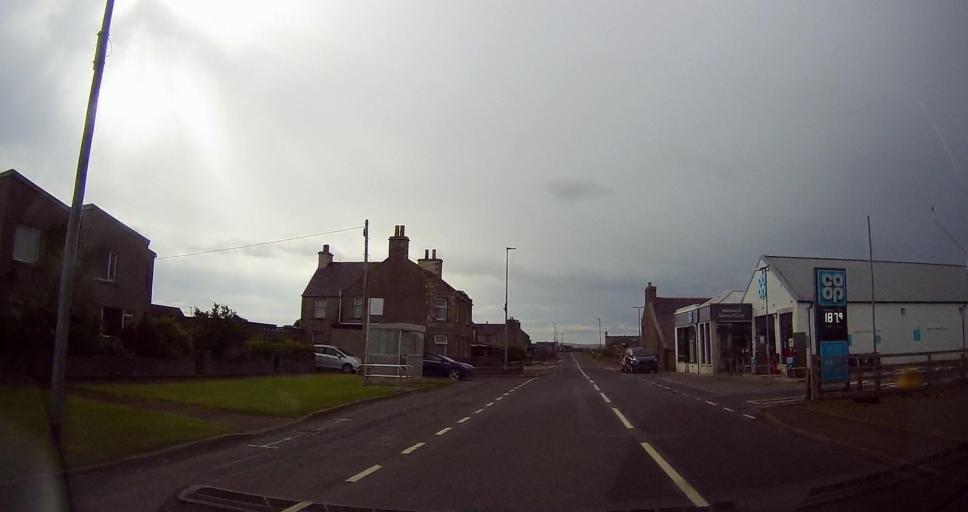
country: GB
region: Scotland
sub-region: Orkney Islands
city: Stromness
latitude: 59.0688
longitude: -3.2320
